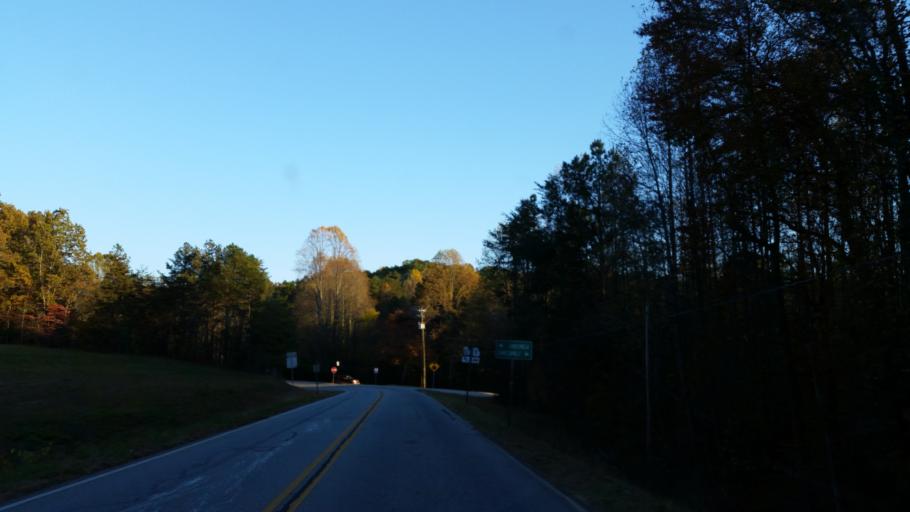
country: US
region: Georgia
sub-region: Lumpkin County
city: Dahlonega
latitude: 34.5209
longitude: -84.0466
